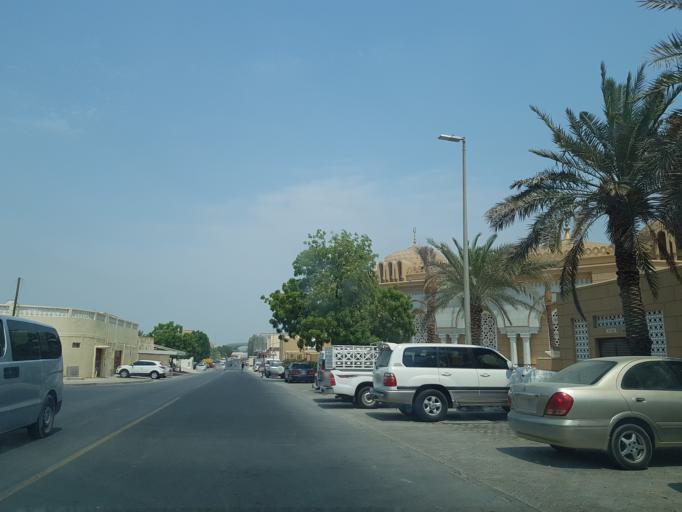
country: AE
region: Ash Shariqah
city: Sharjah
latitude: 25.2332
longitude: 55.3830
